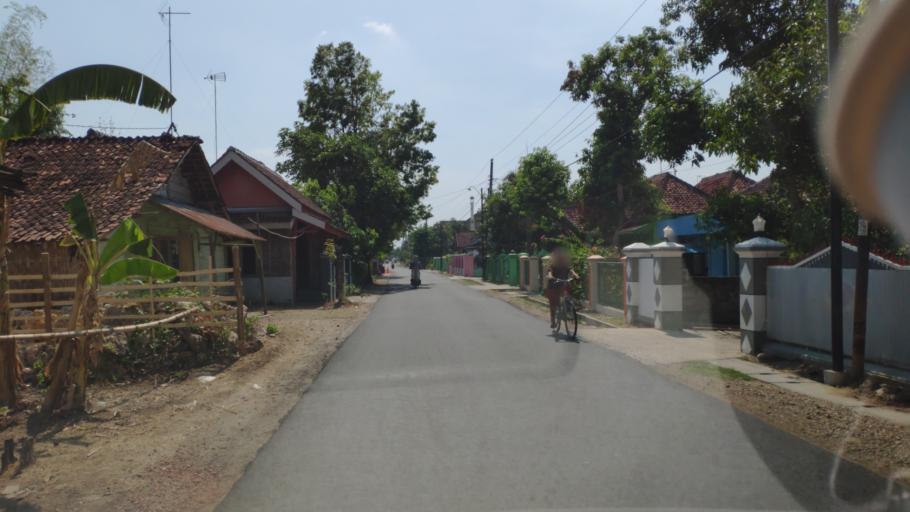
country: ID
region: Central Java
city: Beran
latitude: -6.9787
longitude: 111.4142
